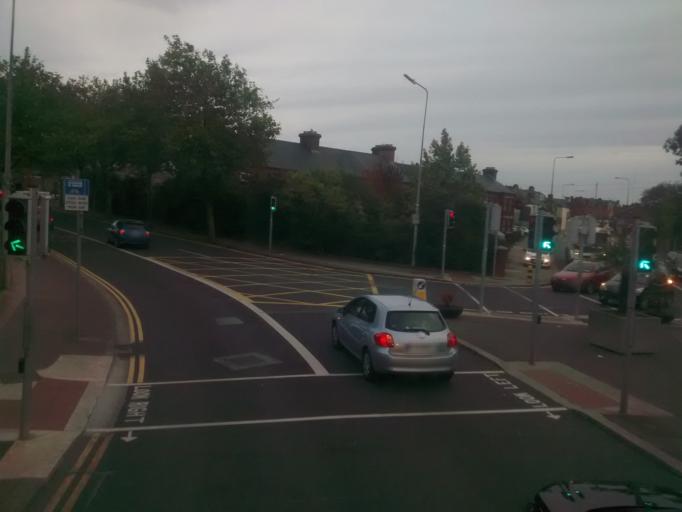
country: IE
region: Leinster
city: Glasnevin
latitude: 53.3676
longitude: -6.2728
